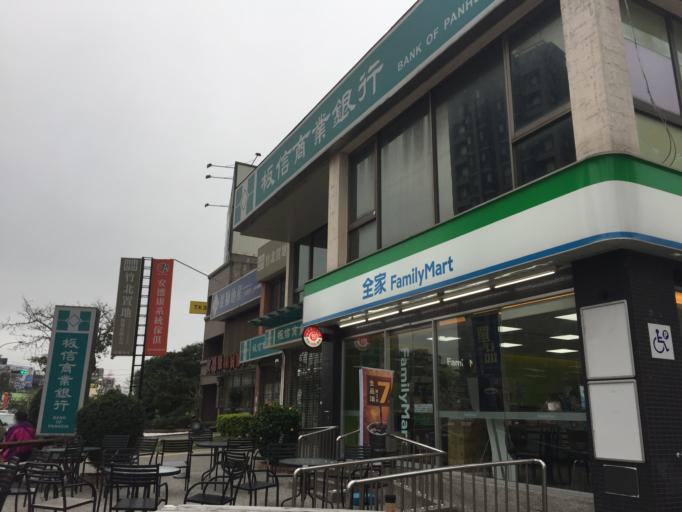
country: TW
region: Taiwan
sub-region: Hsinchu
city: Zhubei
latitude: 24.8186
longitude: 121.0269
